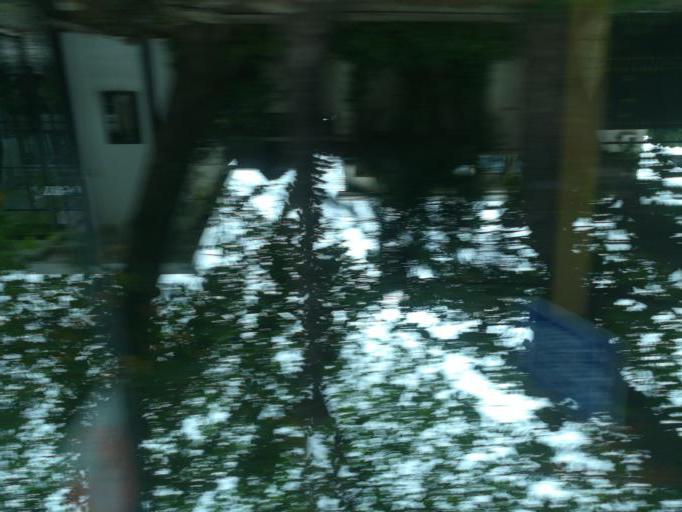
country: NG
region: Lagos
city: Ikoyi
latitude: 6.4252
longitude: 3.4237
